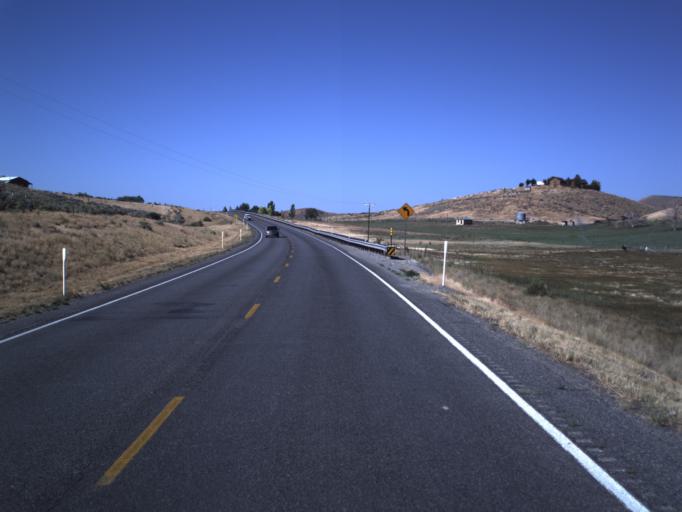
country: US
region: Utah
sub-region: Sanpete County
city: Manti
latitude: 39.2167
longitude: -111.6846
